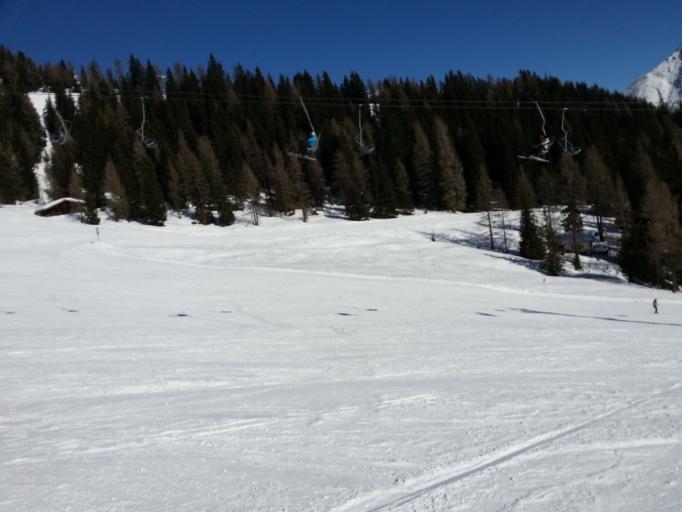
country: AT
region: Salzburg
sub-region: Politischer Bezirk Sankt Johann im Pongau
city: Untertauern
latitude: 47.2926
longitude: 13.4392
